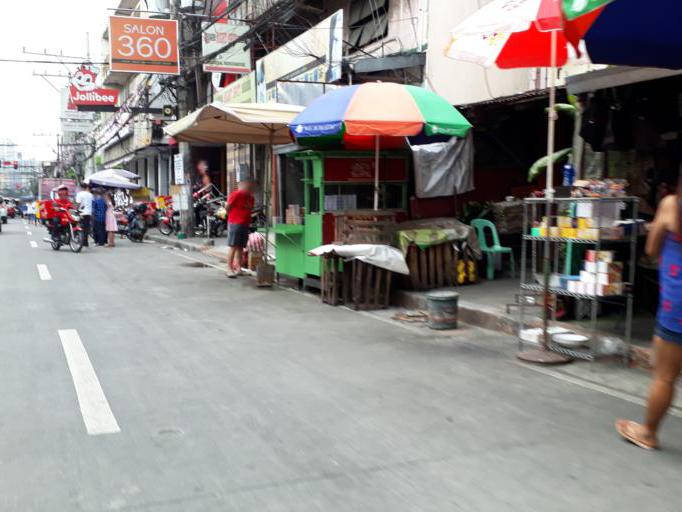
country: PH
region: Metro Manila
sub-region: City of Manila
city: Manila
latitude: 14.6104
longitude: 120.9952
